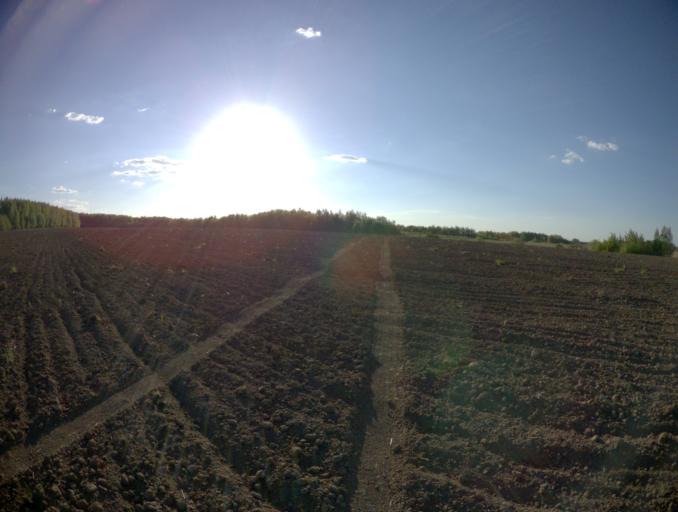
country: RU
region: Ivanovo
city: Gavrilov Posad
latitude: 56.3898
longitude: 40.1173
